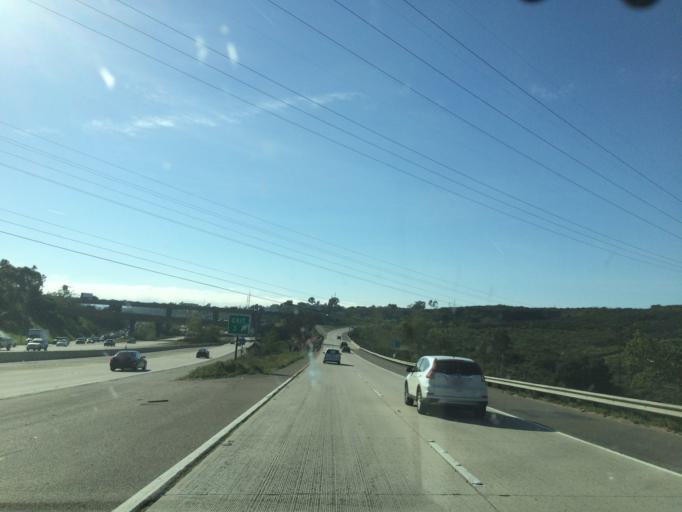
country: US
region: California
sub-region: San Diego County
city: La Jolla
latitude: 32.8466
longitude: -117.1714
